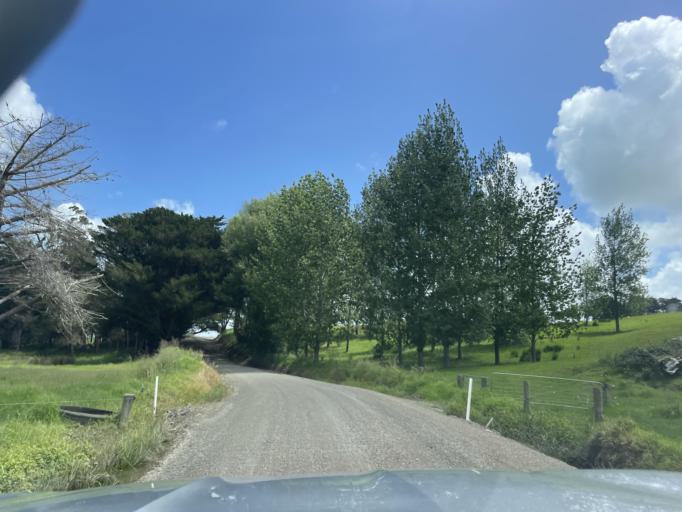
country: NZ
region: Auckland
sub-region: Auckland
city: Wellsford
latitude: -36.1926
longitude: 174.3287
